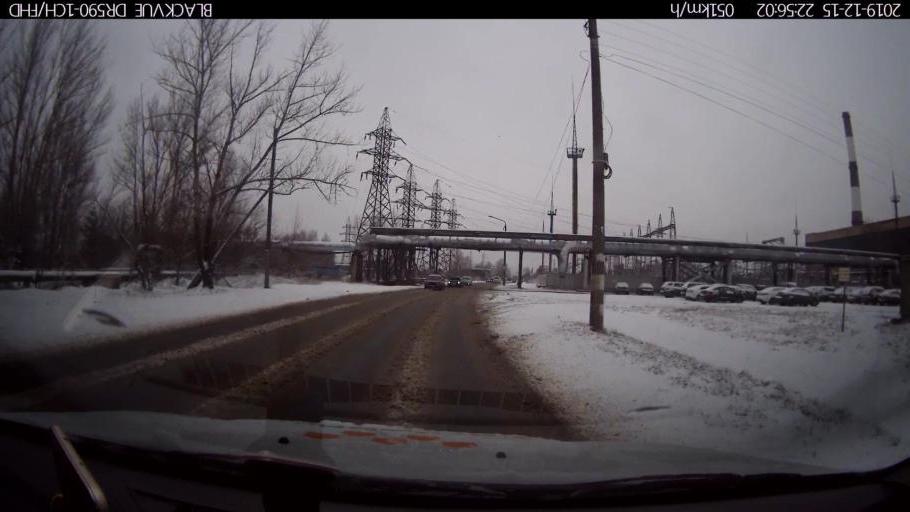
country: RU
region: Nizjnij Novgorod
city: Neklyudovo
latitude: 56.3531
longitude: 43.8954
